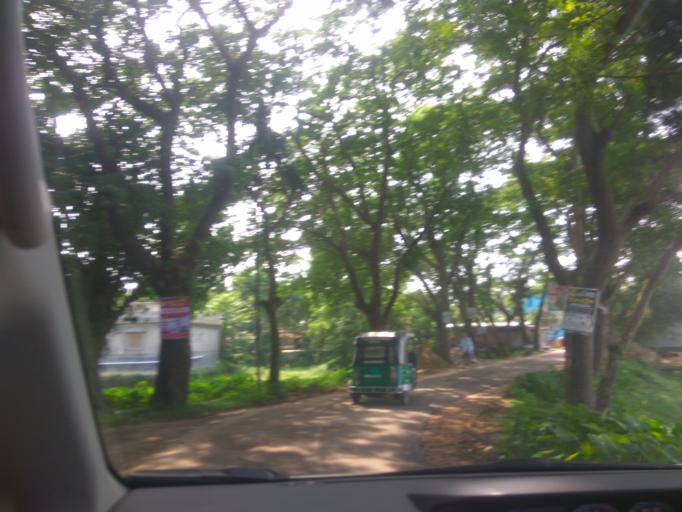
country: IN
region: Assam
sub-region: Karimganj
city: Karimganj
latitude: 24.8091
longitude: 92.1837
